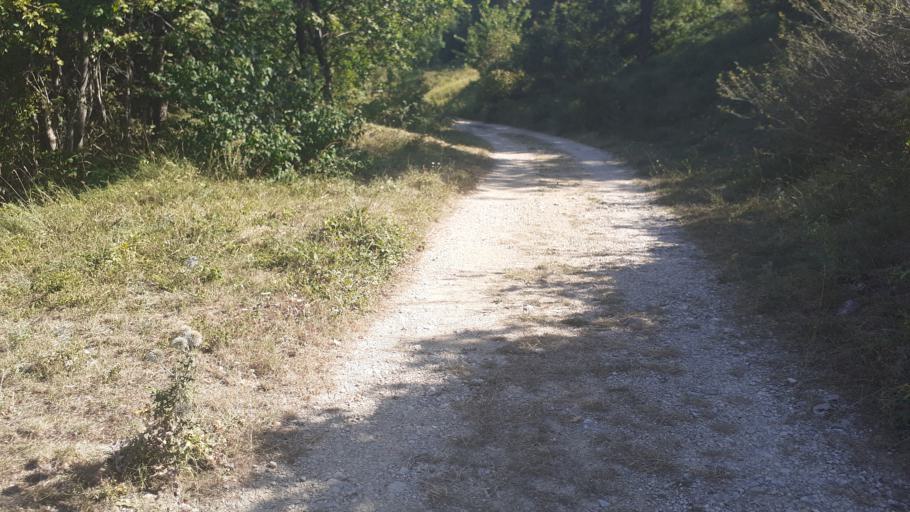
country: IT
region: Abruzzo
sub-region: Provincia di Pescara
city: Sant'Eufemia a Maiella
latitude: 42.1035
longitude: 14.0087
